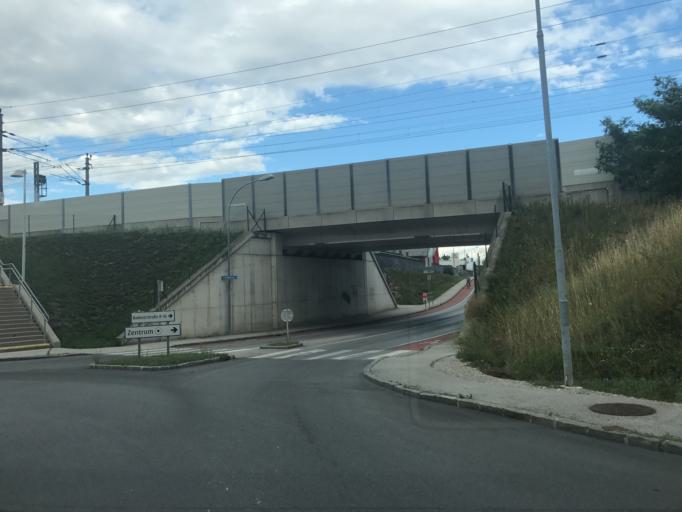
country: AT
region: Lower Austria
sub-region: Politischer Bezirk Wiener Neustadt
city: Theresienfeld
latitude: 47.8340
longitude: 16.2382
